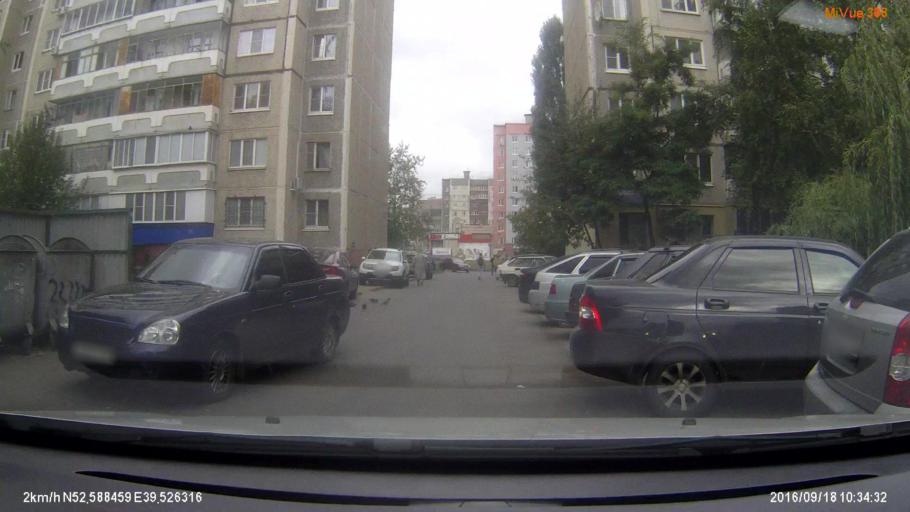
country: RU
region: Lipetsk
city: Syrskoye
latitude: 52.5887
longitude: 39.5300
